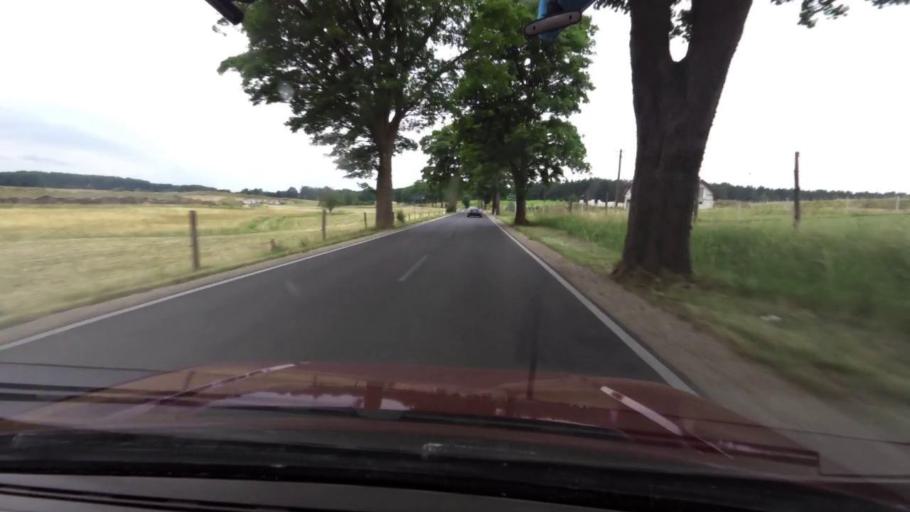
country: PL
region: West Pomeranian Voivodeship
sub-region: Powiat koszalinski
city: Sianow
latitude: 54.1667
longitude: 16.4353
